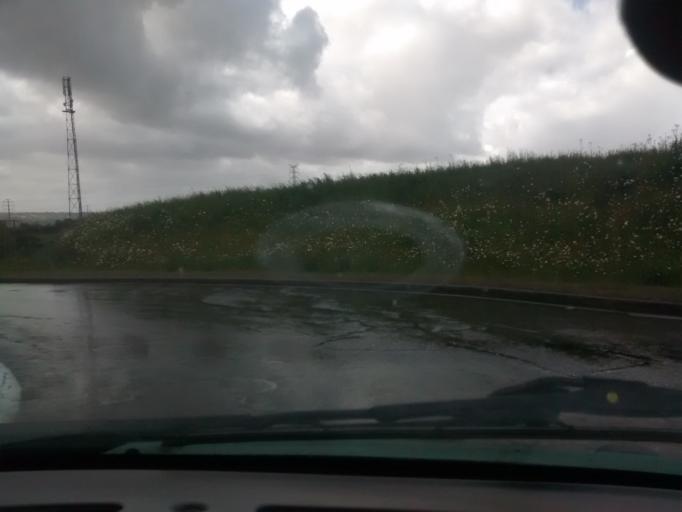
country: FR
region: Lower Normandy
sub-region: Departement de la Manche
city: Conde-sur-Vire
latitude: 49.0734
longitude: -1.0281
